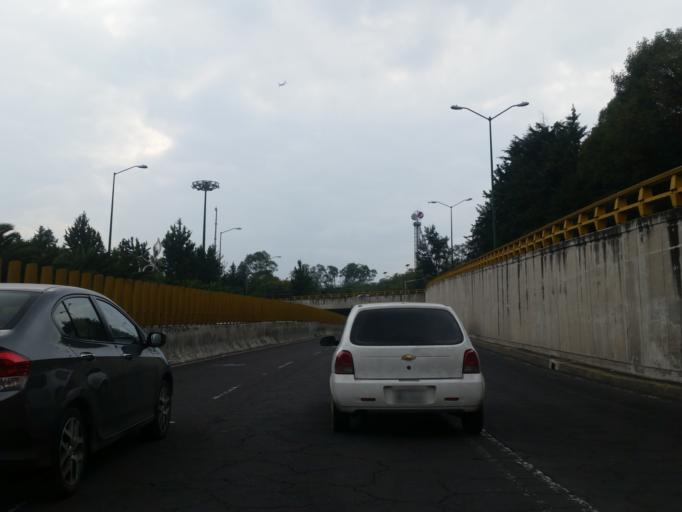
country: MX
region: Mexico City
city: Polanco
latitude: 19.4197
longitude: -99.1930
